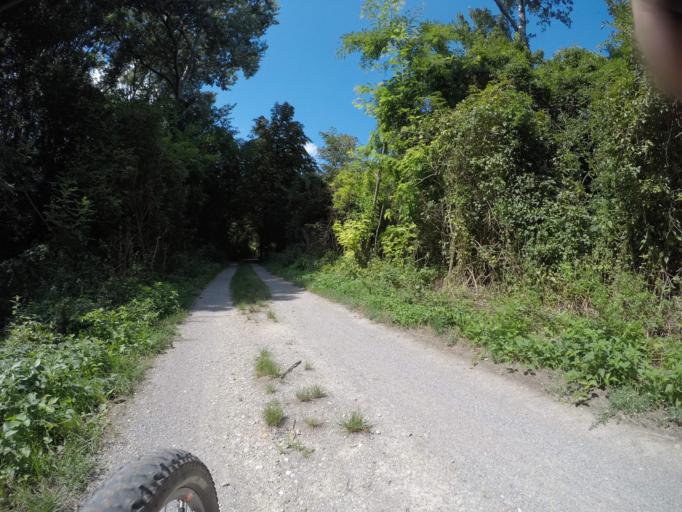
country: AT
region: Lower Austria
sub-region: Politischer Bezirk Ganserndorf
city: Gross-Enzersdorf
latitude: 48.1781
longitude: 16.5130
